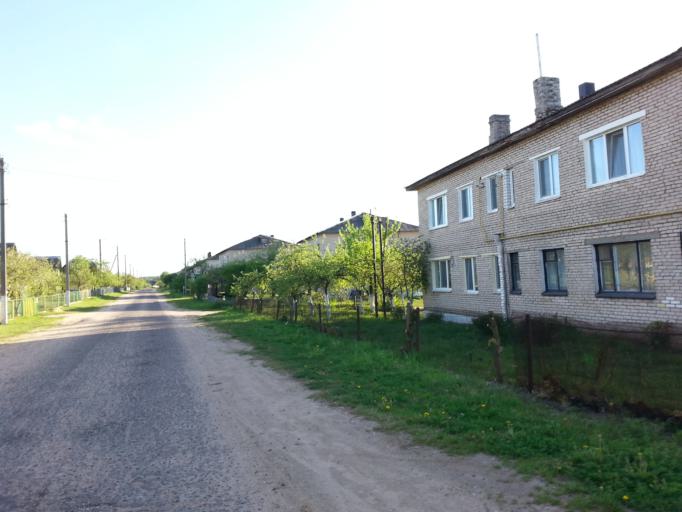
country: BY
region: Minsk
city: Narach
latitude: 54.9358
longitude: 26.6929
